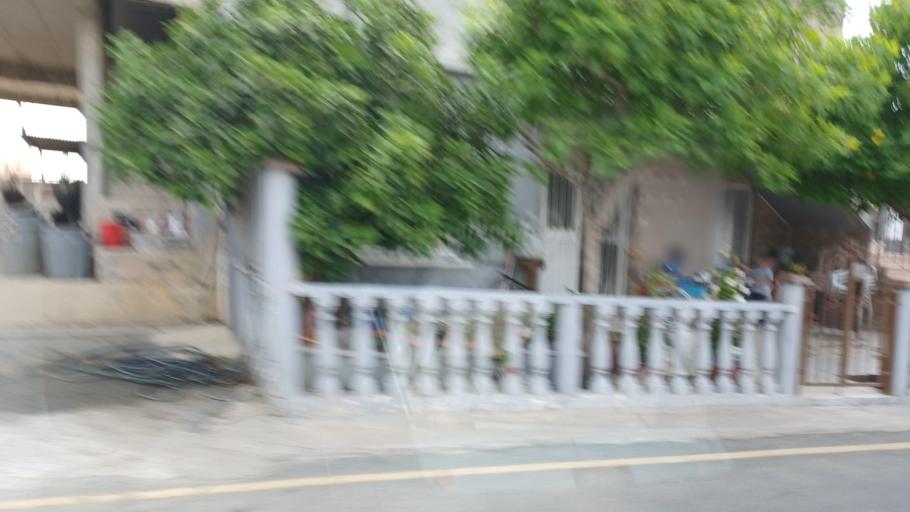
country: CY
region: Ammochostos
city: Deryneia
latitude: 35.0599
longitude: 33.9587
